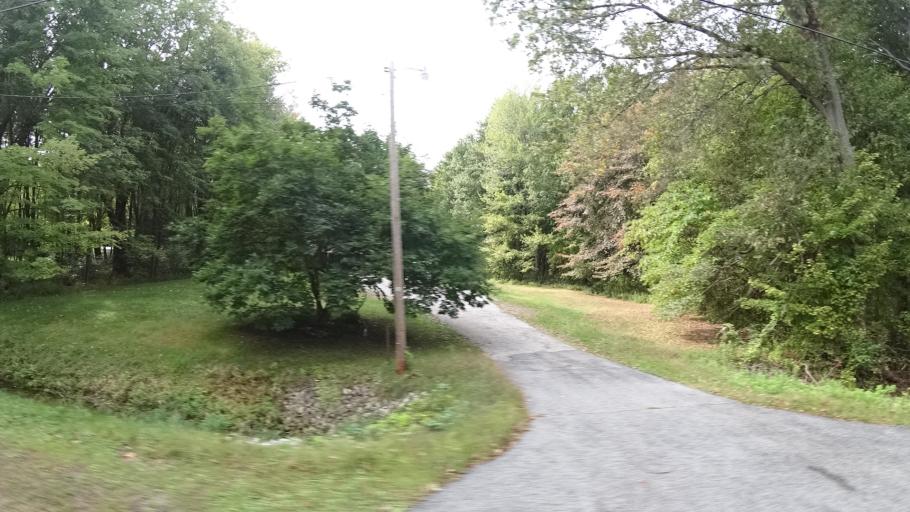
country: US
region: Indiana
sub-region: LaPorte County
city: Long Beach
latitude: 41.7376
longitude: -86.8362
